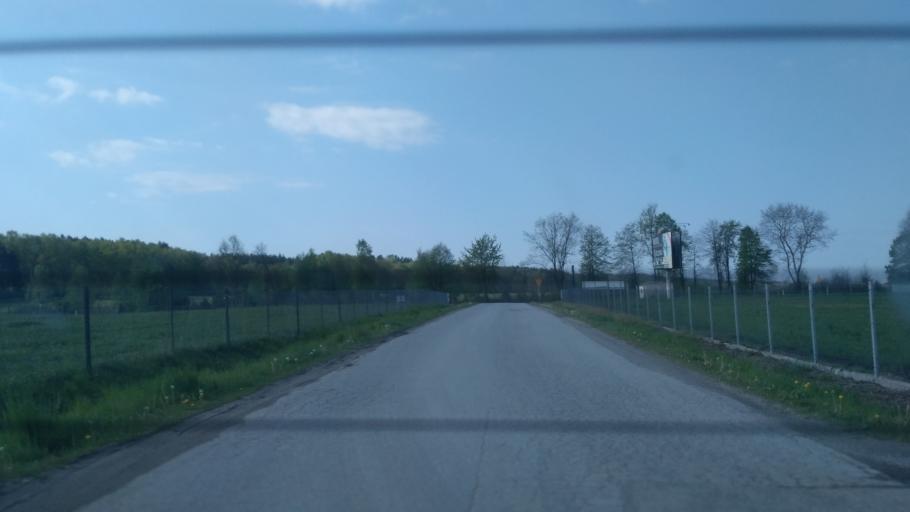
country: PL
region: Subcarpathian Voivodeship
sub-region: Powiat lubaczowski
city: Wielkie Oczy
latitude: 49.9696
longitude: 23.0598
